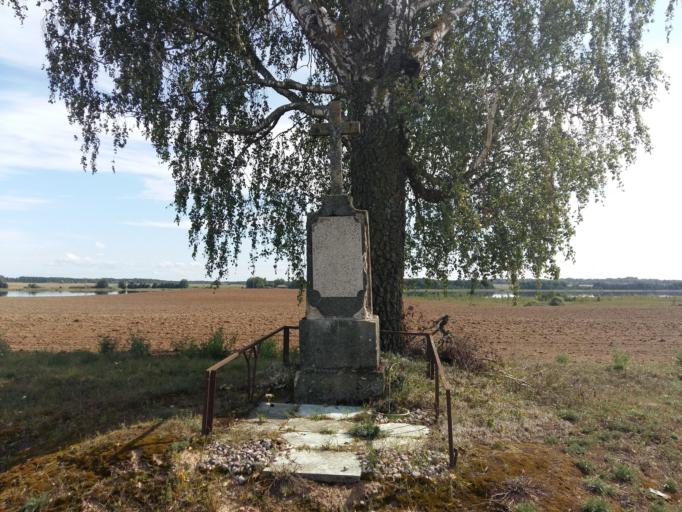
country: LT
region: Marijampoles apskritis
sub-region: Marijampole Municipality
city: Marijampole
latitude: 54.4090
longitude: 23.4078
